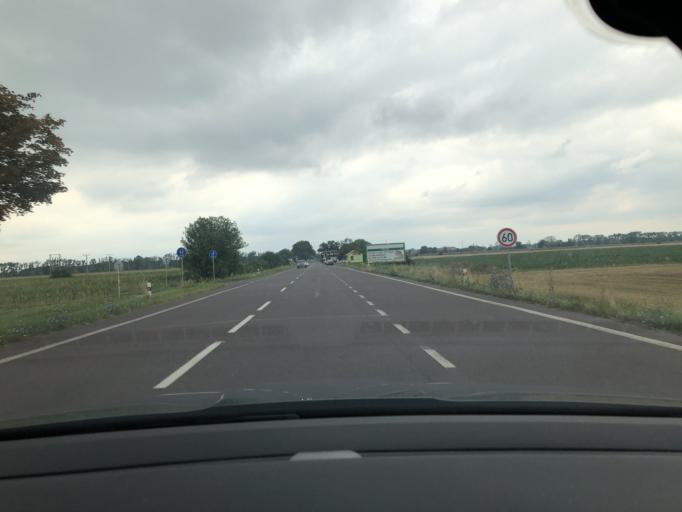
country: CZ
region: South Moravian
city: Hevlin
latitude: 48.7366
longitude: 16.3824
